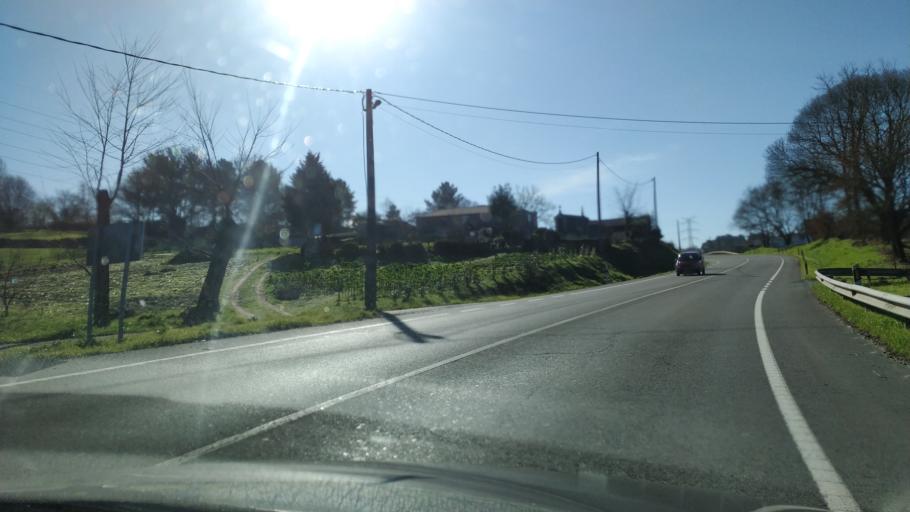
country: ES
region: Galicia
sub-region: Provincia de Pontevedra
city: Silleda
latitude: 42.7150
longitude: -8.2800
